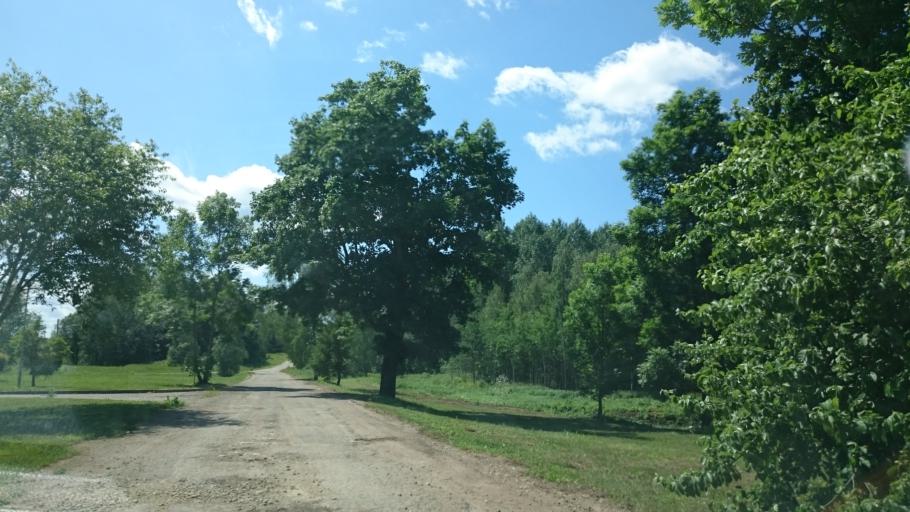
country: LV
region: Cibla
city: Cibla
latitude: 56.5935
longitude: 27.9890
